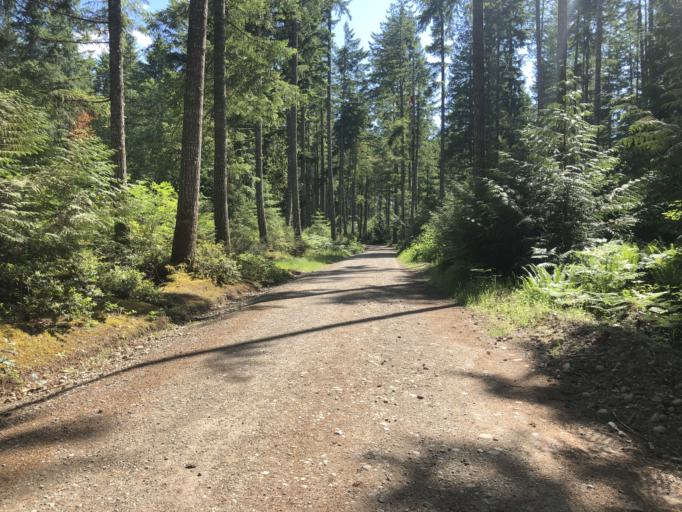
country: US
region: Washington
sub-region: Kitsap County
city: Erlands Point-Kitsap Lake
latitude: 47.5785
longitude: -122.7232
